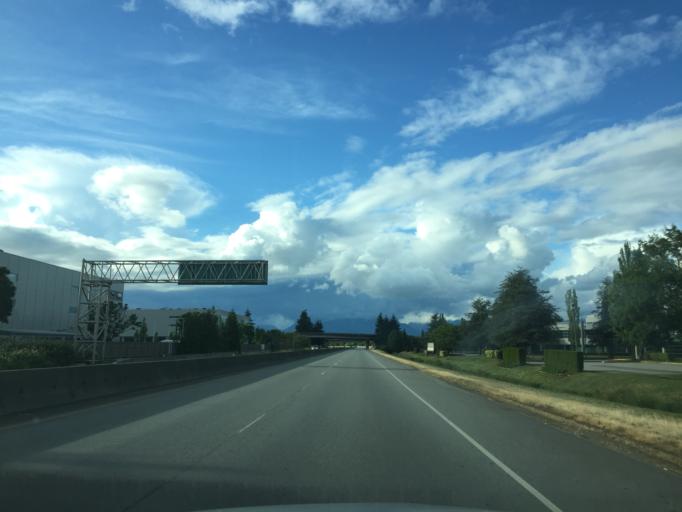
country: CA
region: British Columbia
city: Richmond
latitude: 49.1725
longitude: -123.0744
